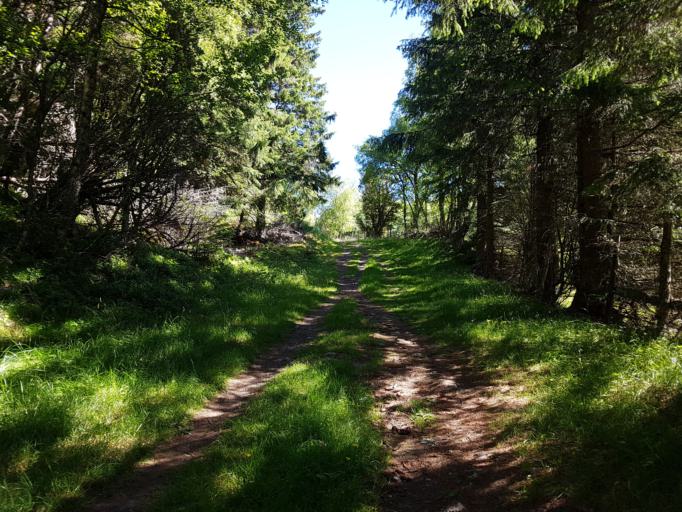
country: NO
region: Sor-Trondelag
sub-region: Skaun
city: Borsa
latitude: 63.4311
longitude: 10.1950
